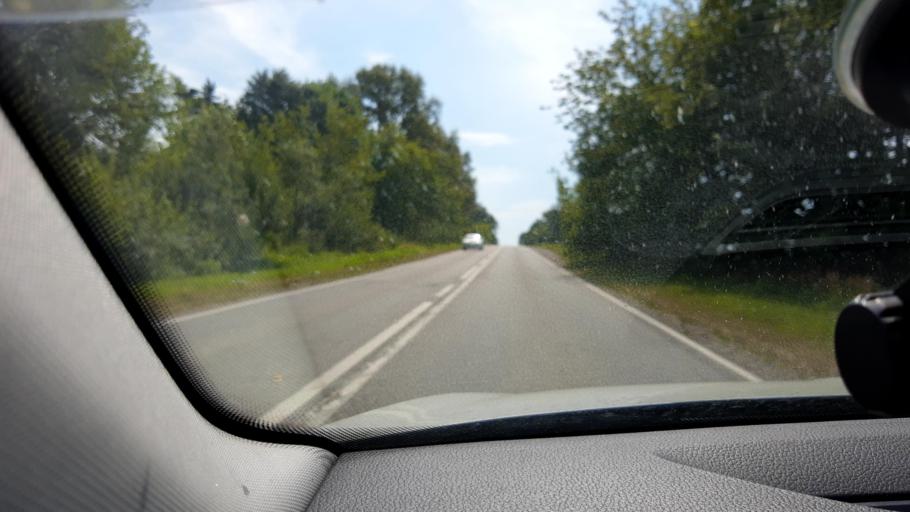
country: RU
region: Tula
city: Zaokskiy
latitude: 54.7712
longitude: 37.4359
